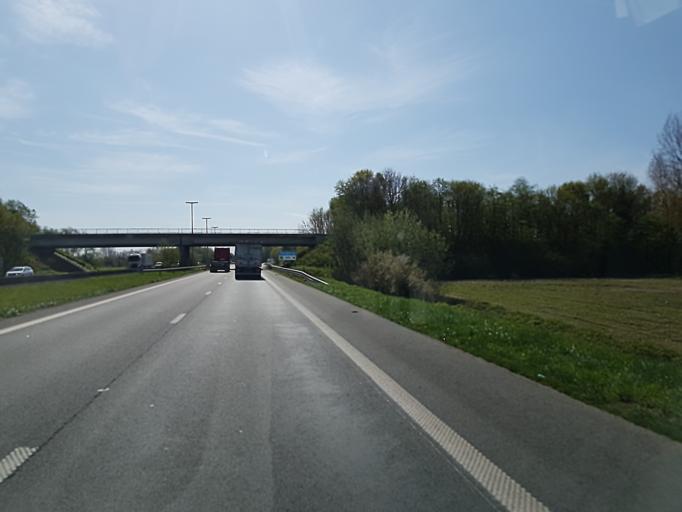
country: FR
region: Nord-Pas-de-Calais
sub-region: Departement du Nord
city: Leers
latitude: 50.6542
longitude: 3.2910
